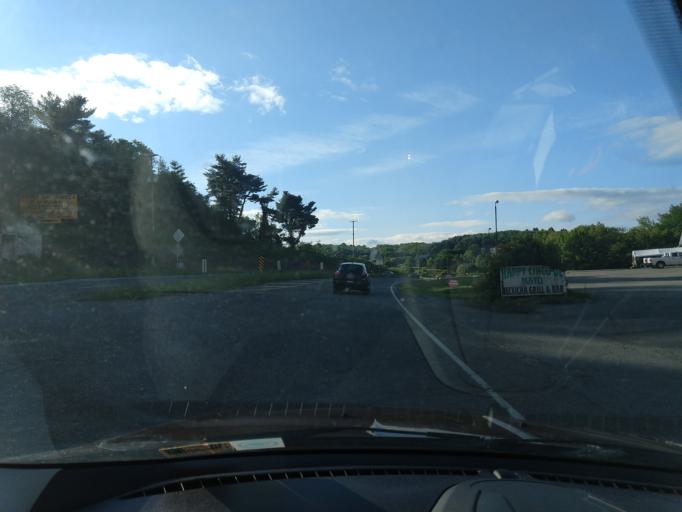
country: US
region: Virginia
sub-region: Wythe County
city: Wytheville
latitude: 36.9420
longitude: -80.9461
